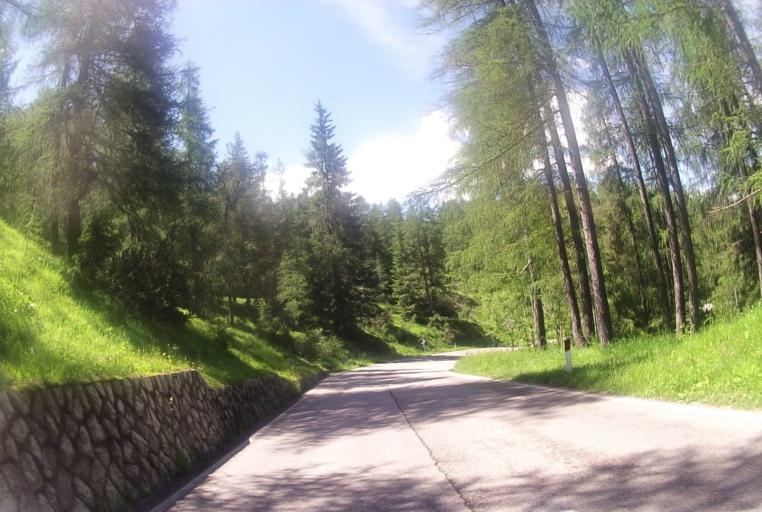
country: IT
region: Veneto
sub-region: Provincia di Belluno
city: Cortina d'Ampezzo
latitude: 46.5431
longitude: 12.1632
